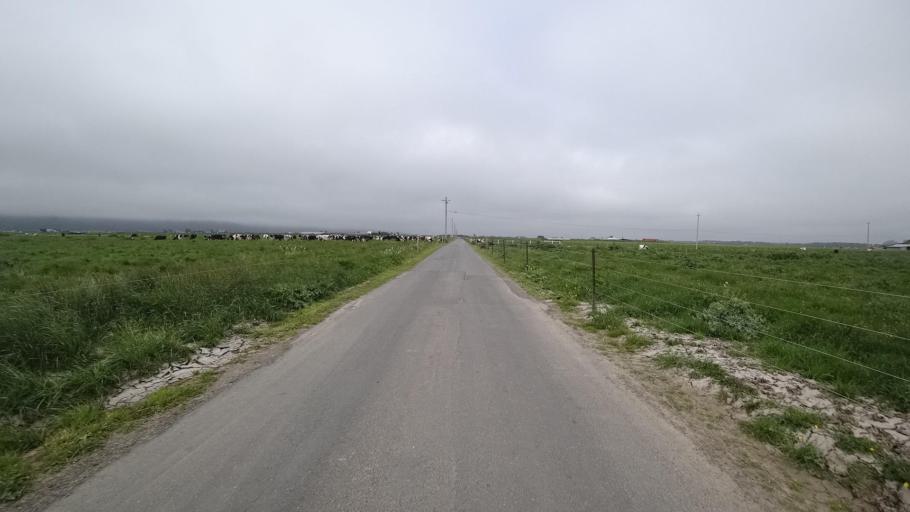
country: US
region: California
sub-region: Humboldt County
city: Fortuna
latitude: 40.5916
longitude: -124.1916
